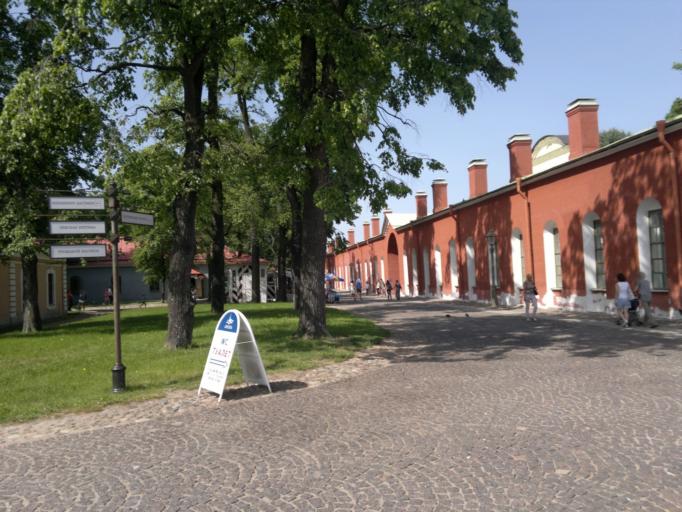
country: RU
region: St.-Petersburg
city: Saint Petersburg
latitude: 59.9502
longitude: 30.3201
